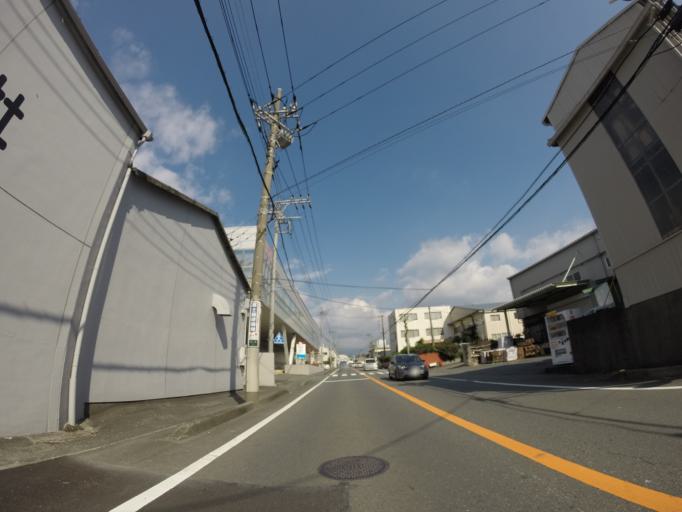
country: JP
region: Shizuoka
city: Fuji
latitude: 35.1819
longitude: 138.6478
